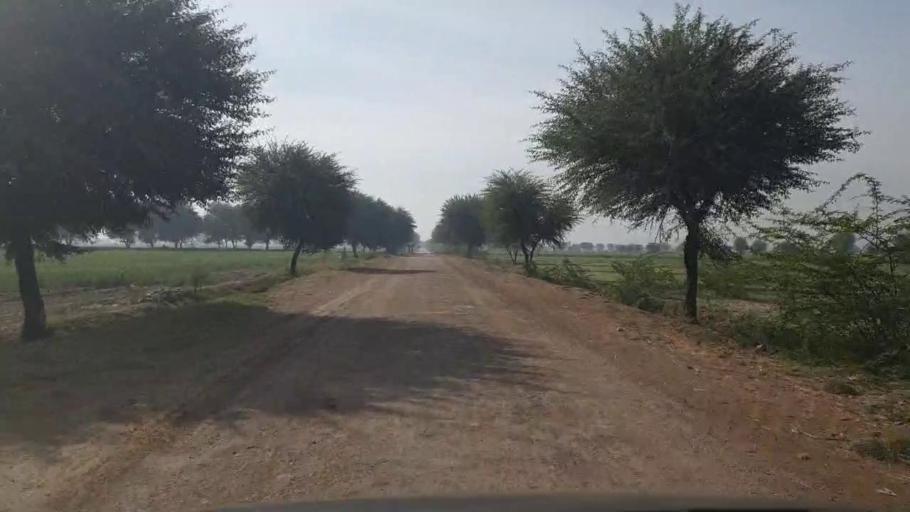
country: PK
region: Sindh
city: Umarkot
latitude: 25.3480
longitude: 69.6762
